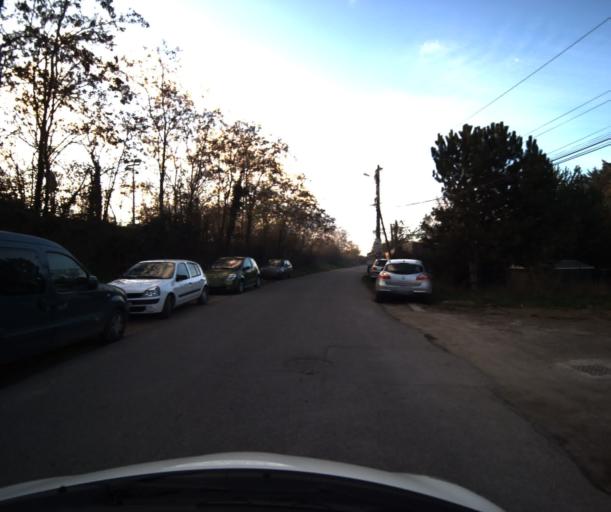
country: FR
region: Provence-Alpes-Cote d'Azur
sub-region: Departement du Vaucluse
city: Pertuis
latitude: 43.6855
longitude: 5.5013
